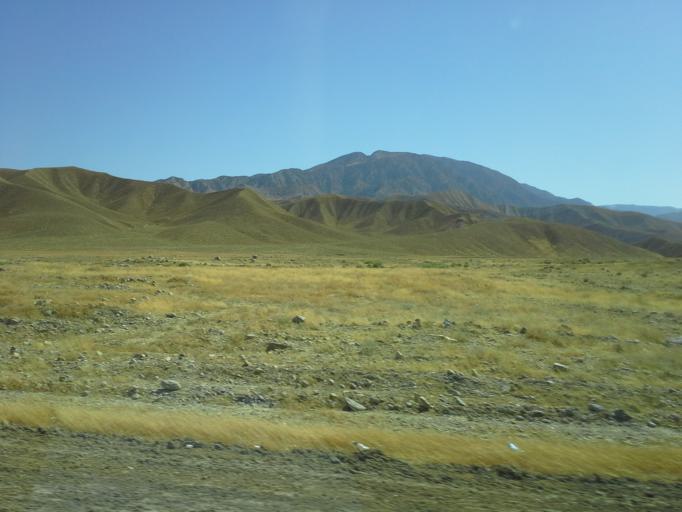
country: TM
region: Ahal
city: Baharly
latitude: 38.6065
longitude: 57.0608
